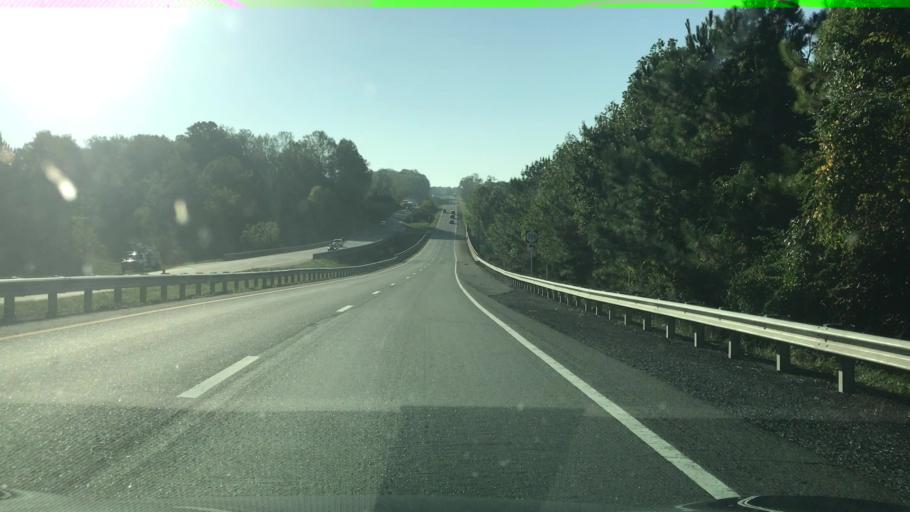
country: US
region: Virginia
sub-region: Bedford County
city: Forest
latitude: 37.3096
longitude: -79.3960
